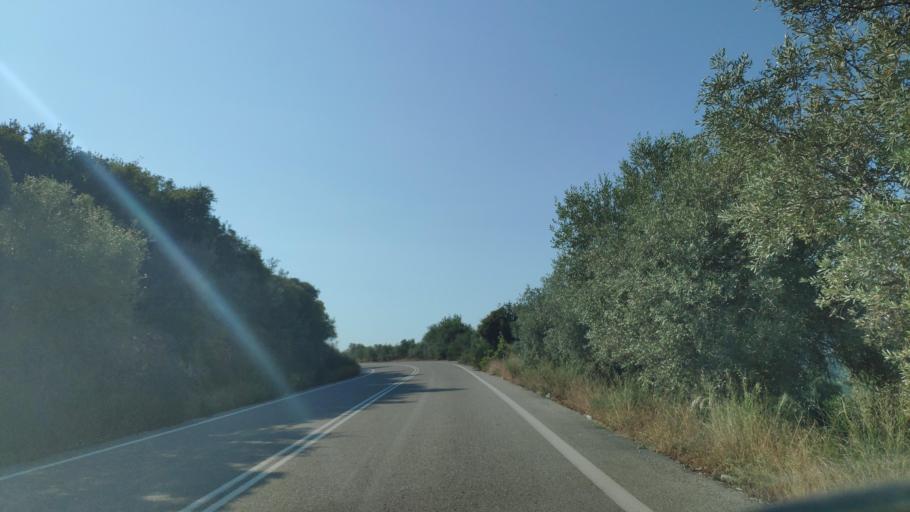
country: GR
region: West Greece
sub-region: Nomos Aitolias kai Akarnanias
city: Stanos
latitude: 38.7711
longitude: 21.1575
